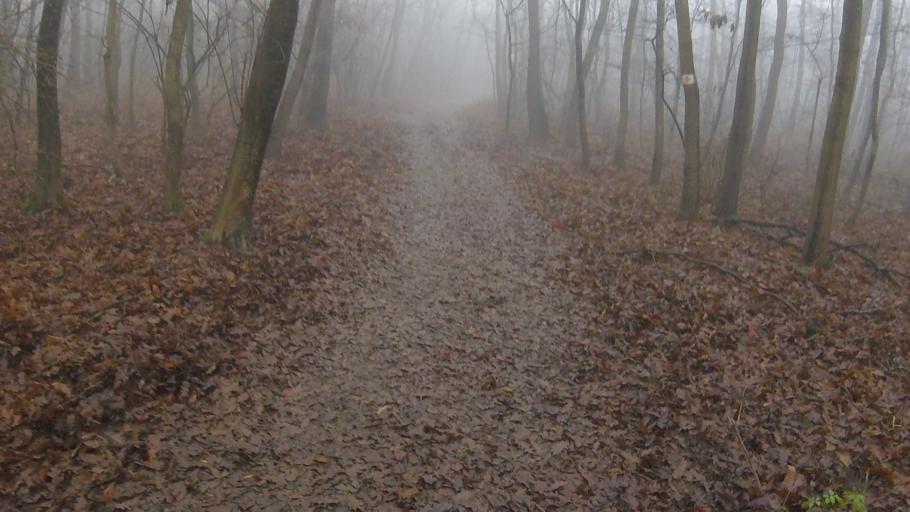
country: HU
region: Pest
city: Budakeszi
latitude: 47.5262
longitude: 18.9346
